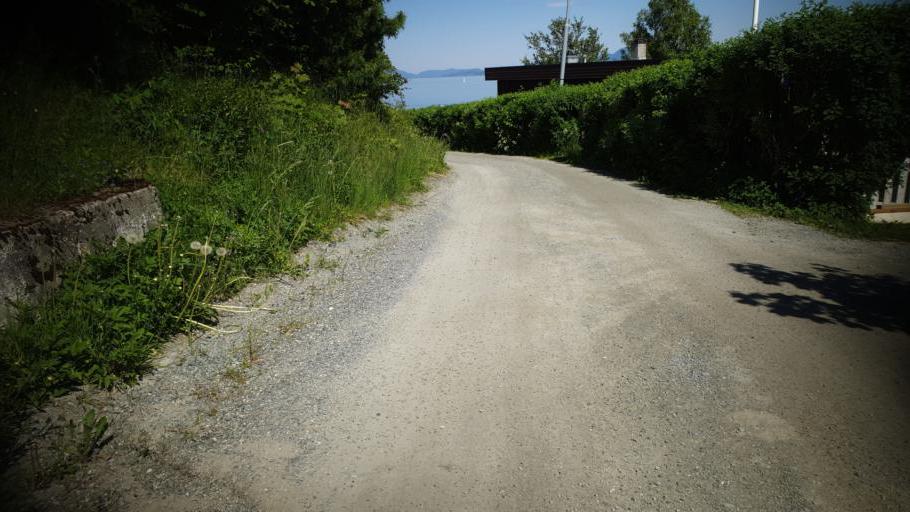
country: NO
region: Sor-Trondelag
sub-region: Malvik
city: Malvik
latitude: 63.4279
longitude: 10.5467
